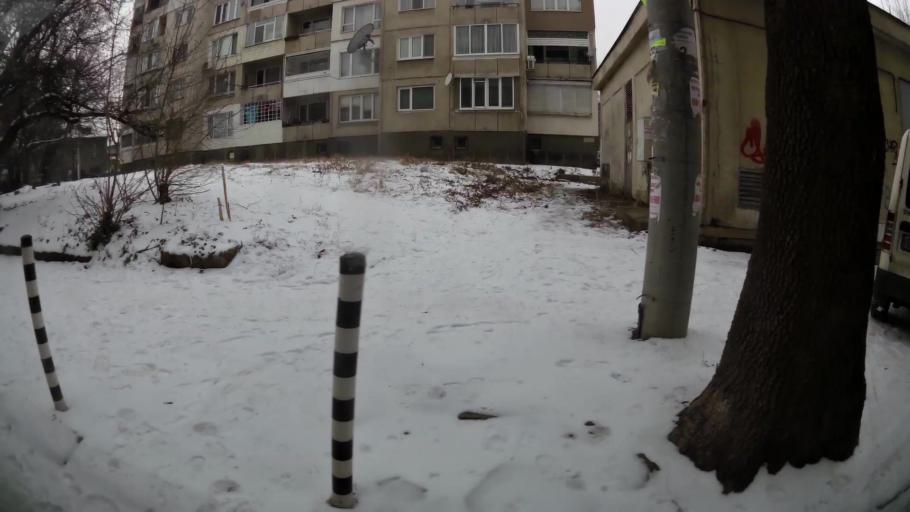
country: BG
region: Sofia-Capital
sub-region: Stolichna Obshtina
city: Sofia
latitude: 42.7079
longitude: 23.3168
